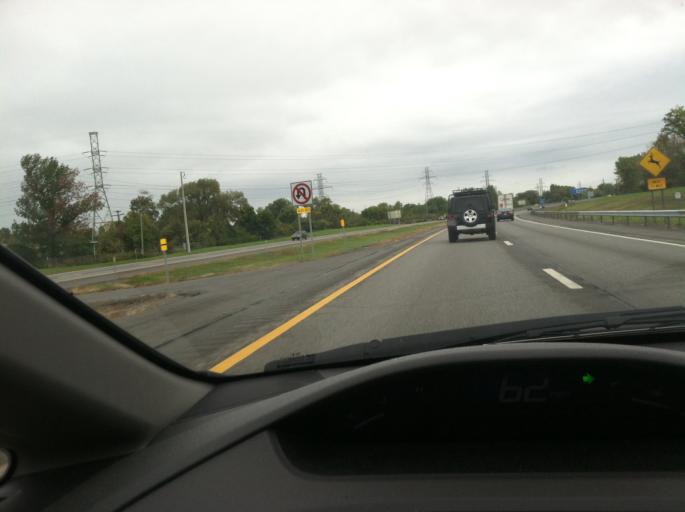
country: US
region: New York
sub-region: Erie County
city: Blasdell
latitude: 42.7920
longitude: -78.8163
